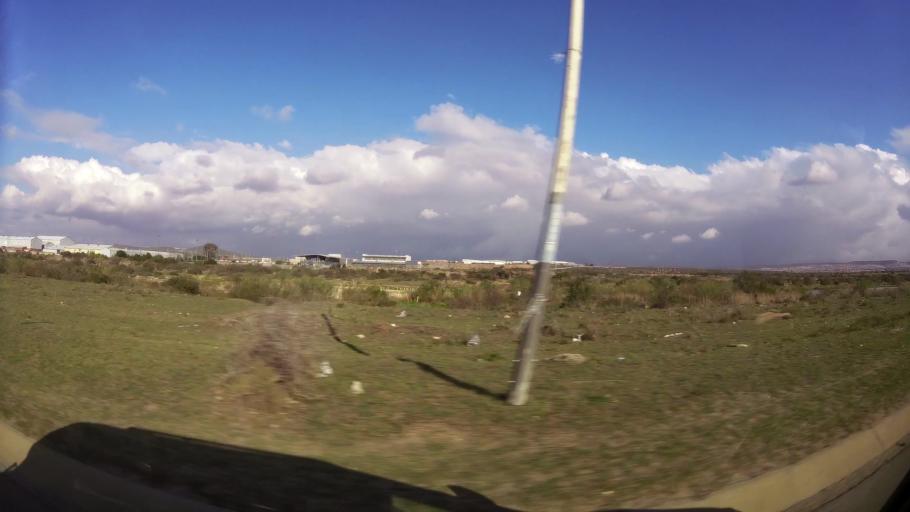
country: ZA
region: Eastern Cape
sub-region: Nelson Mandela Bay Metropolitan Municipality
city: Uitenhage
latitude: -33.7903
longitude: 25.4198
